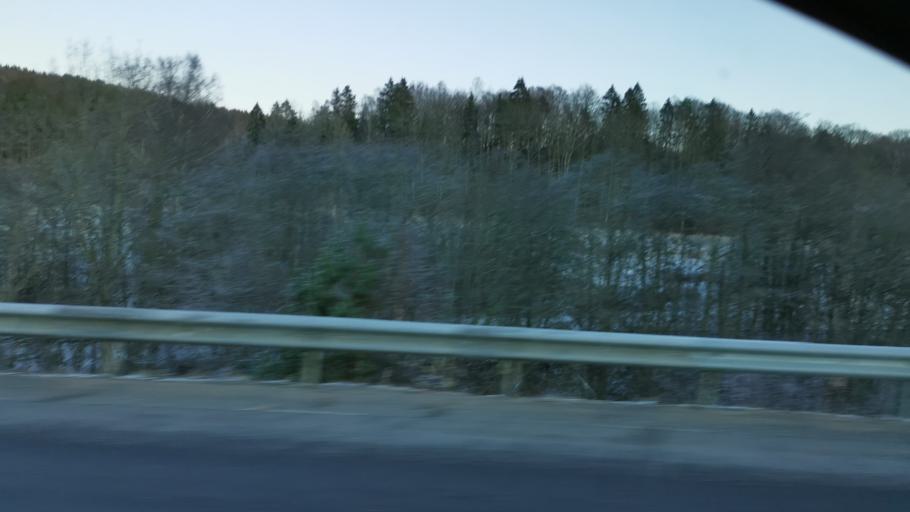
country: SE
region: Vaestra Goetaland
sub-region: Munkedals Kommun
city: Munkedal
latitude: 58.4274
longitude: 11.7226
